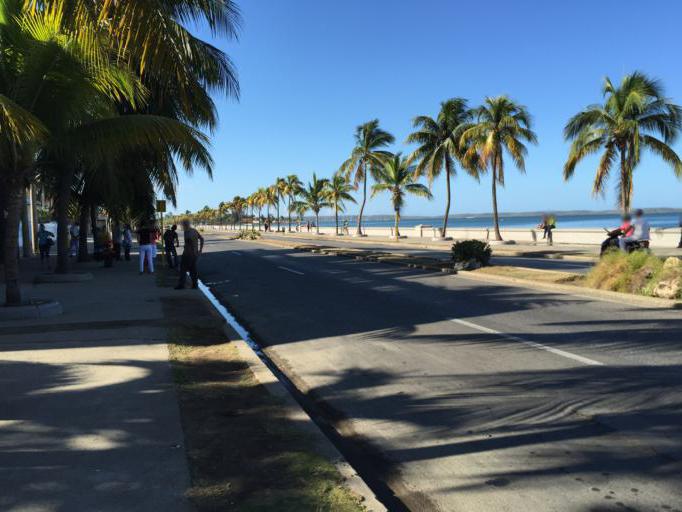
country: CU
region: Cienfuegos
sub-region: Municipio de Cienfuegos
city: Cienfuegos
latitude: 22.1379
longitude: -80.4491
